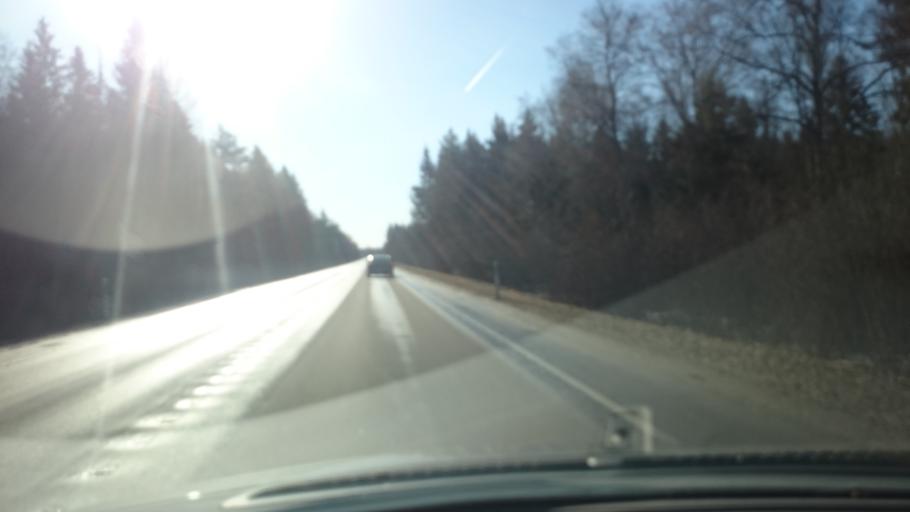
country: EE
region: Raplamaa
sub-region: Kohila vald
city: Kohila
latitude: 59.2408
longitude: 24.7567
